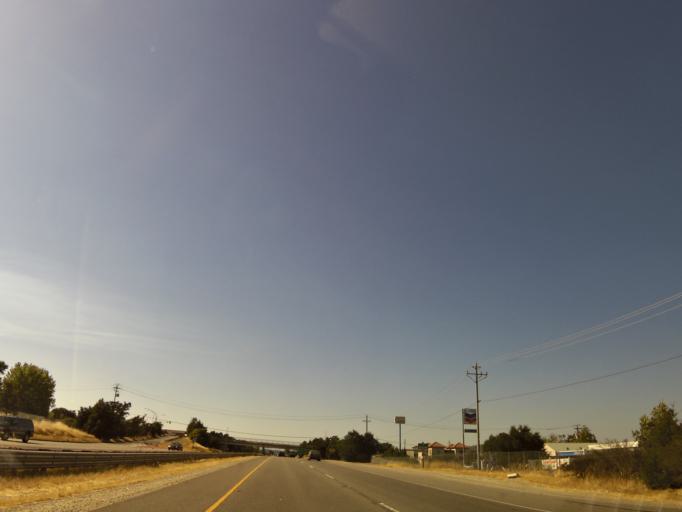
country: US
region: California
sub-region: San Luis Obispo County
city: Atascadero
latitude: 35.4638
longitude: -120.6495
